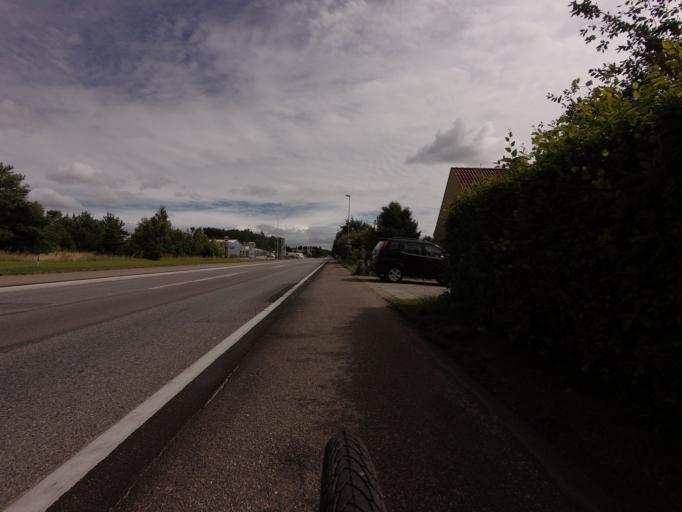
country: DK
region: Central Jutland
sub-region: Syddjurs Kommune
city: Ryomgard
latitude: 56.3824
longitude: 10.4851
